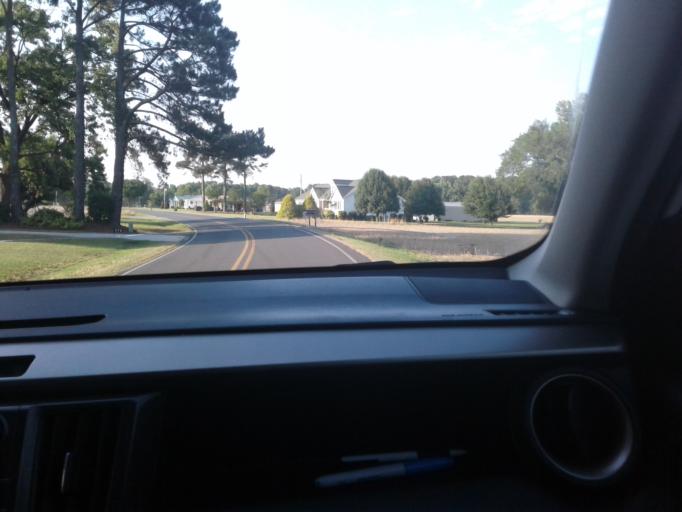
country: US
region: North Carolina
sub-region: Harnett County
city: Dunn
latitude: 35.3352
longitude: -78.5766
